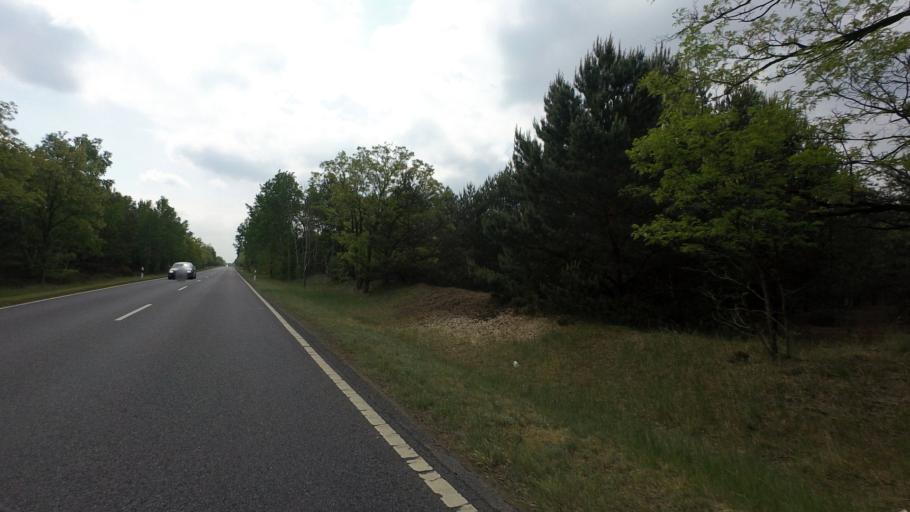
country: DE
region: Brandenburg
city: Drachhausen
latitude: 51.9468
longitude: 14.3357
